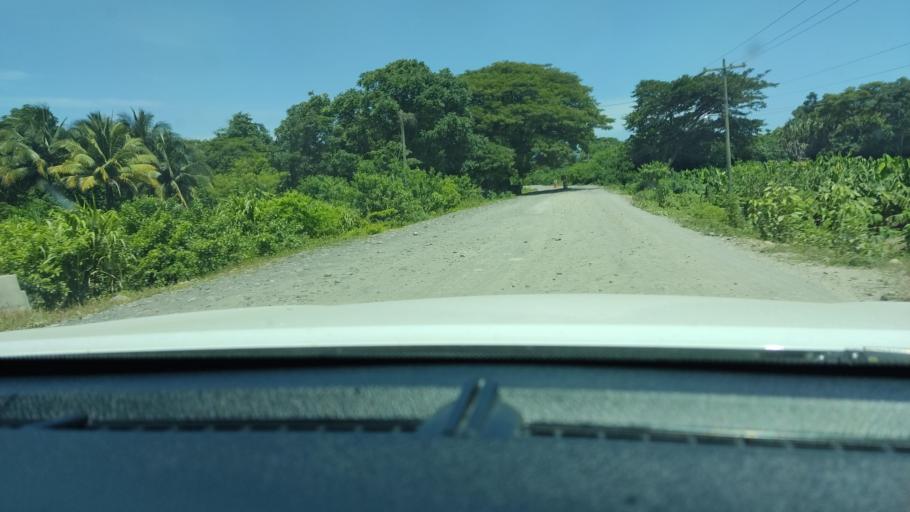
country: SV
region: Ahuachapan
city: San Francisco Menendez
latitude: 13.7849
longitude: -90.1185
